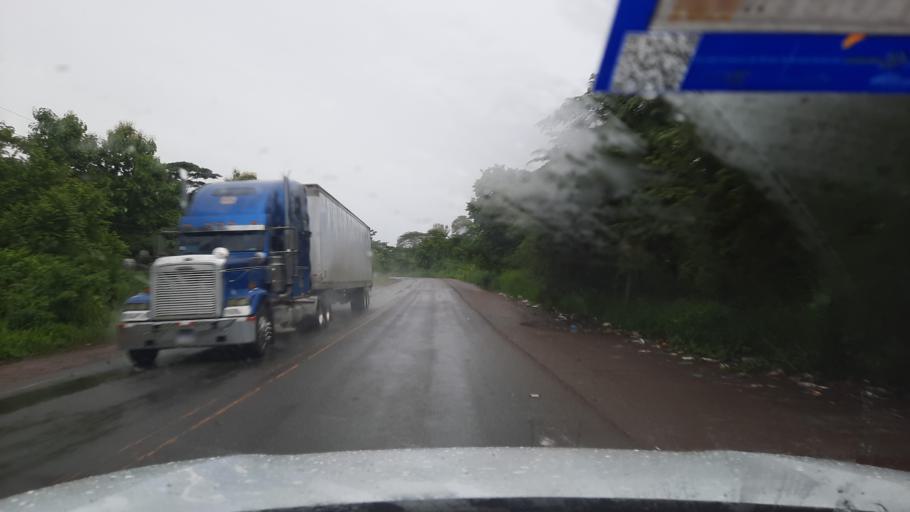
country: NI
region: Rivas
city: Cardenas
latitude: 11.1869
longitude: -85.6198
